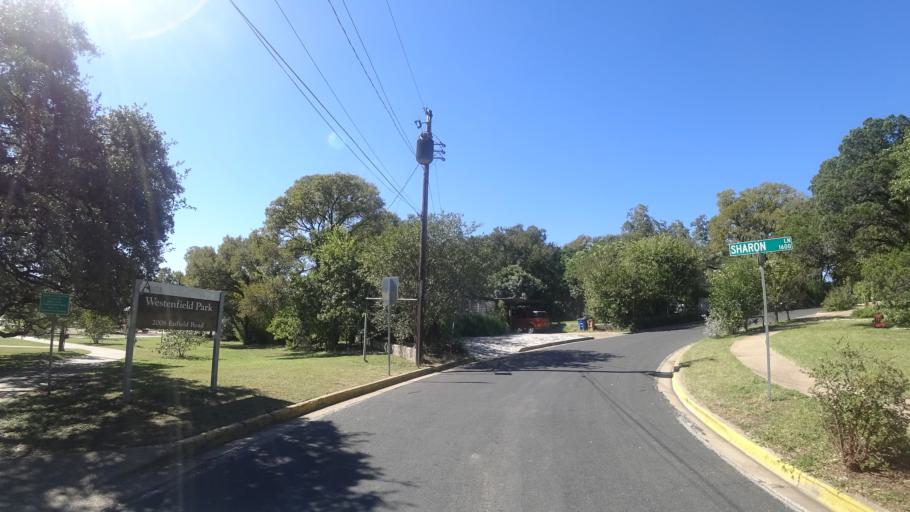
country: US
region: Texas
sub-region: Travis County
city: Rollingwood
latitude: 30.2883
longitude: -97.7644
